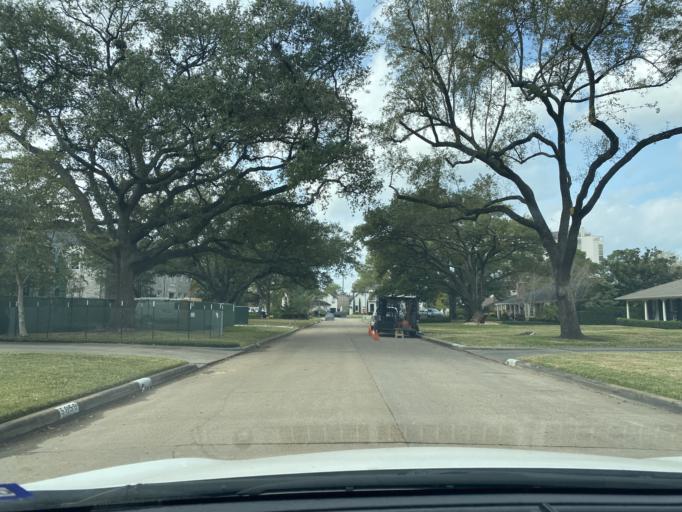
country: US
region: Texas
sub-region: Harris County
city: Hunters Creek Village
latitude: 29.7536
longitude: -95.4759
